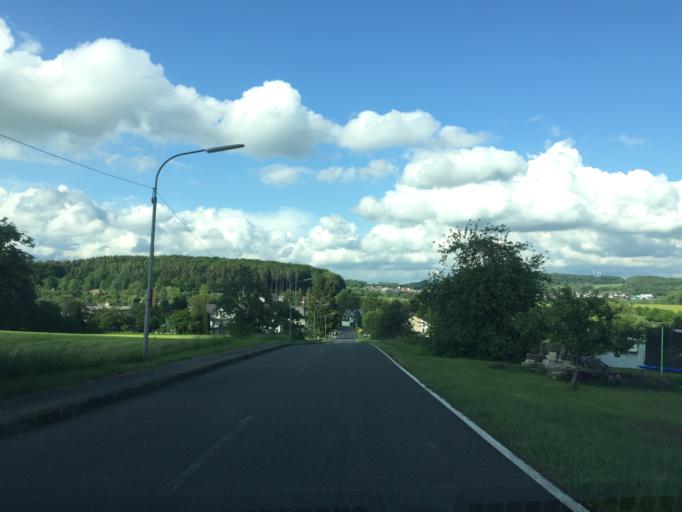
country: DE
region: Rheinland-Pfalz
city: Meudt
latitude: 50.4969
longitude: 7.9017
